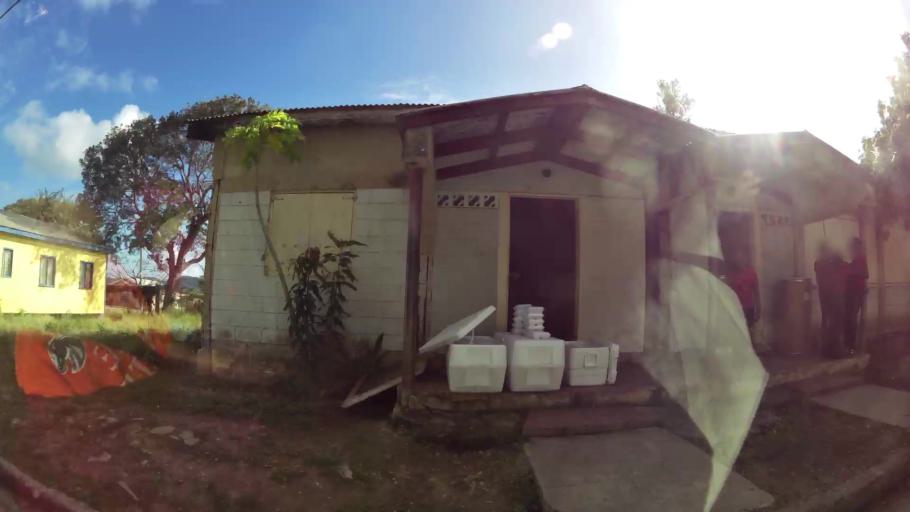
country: AG
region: Saint Peter
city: All Saints
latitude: 17.0640
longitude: -61.7944
